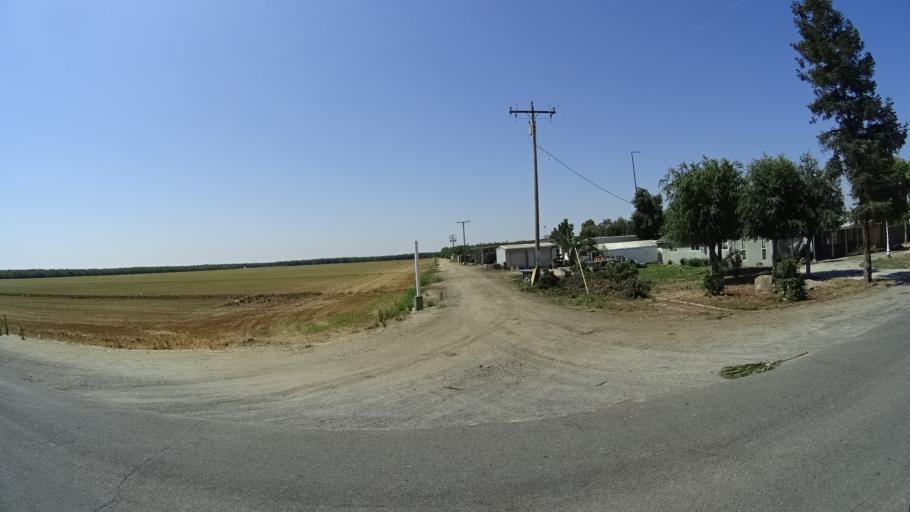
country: US
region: California
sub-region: Kings County
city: Lucerne
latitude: 36.3718
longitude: -119.6046
